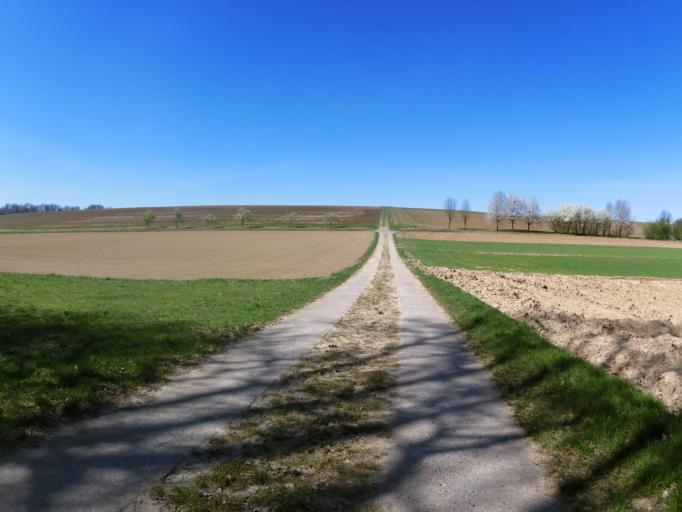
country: DE
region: Bavaria
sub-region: Regierungsbezirk Unterfranken
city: Rottendorf
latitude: 49.8106
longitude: 10.0745
